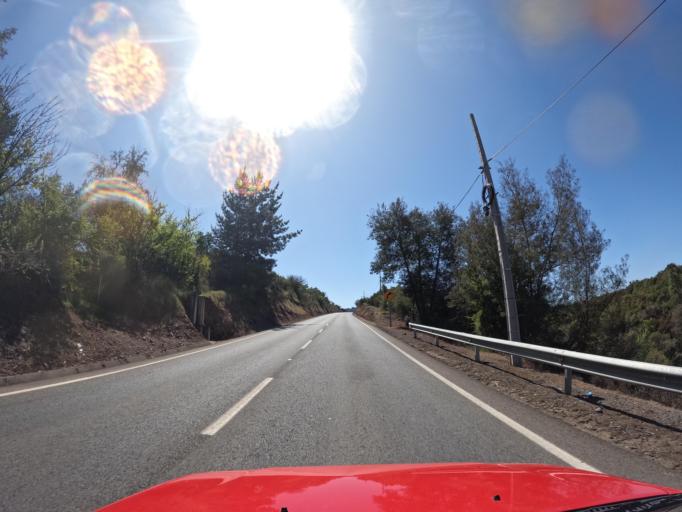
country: CL
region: Maule
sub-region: Provincia de Talca
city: San Clemente
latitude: -35.4528
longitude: -71.2696
